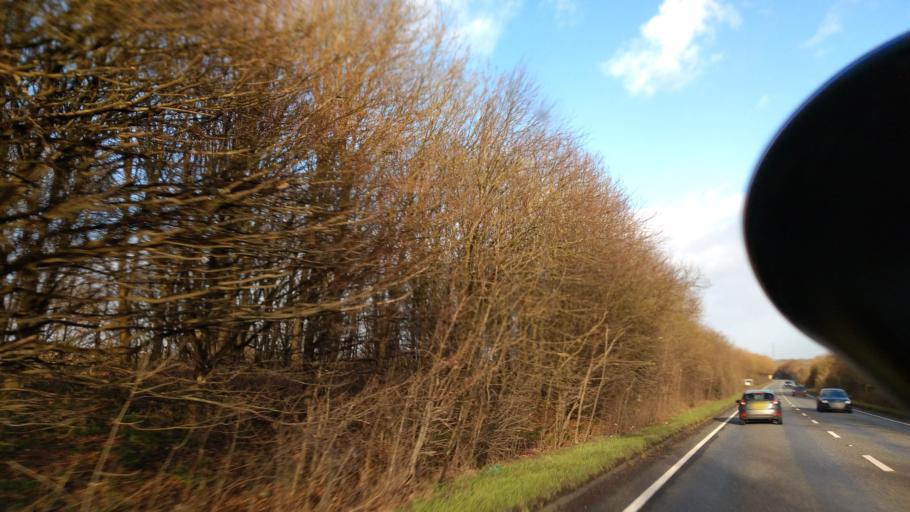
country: GB
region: England
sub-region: Somerset
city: Frome
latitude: 51.2119
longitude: -2.3120
